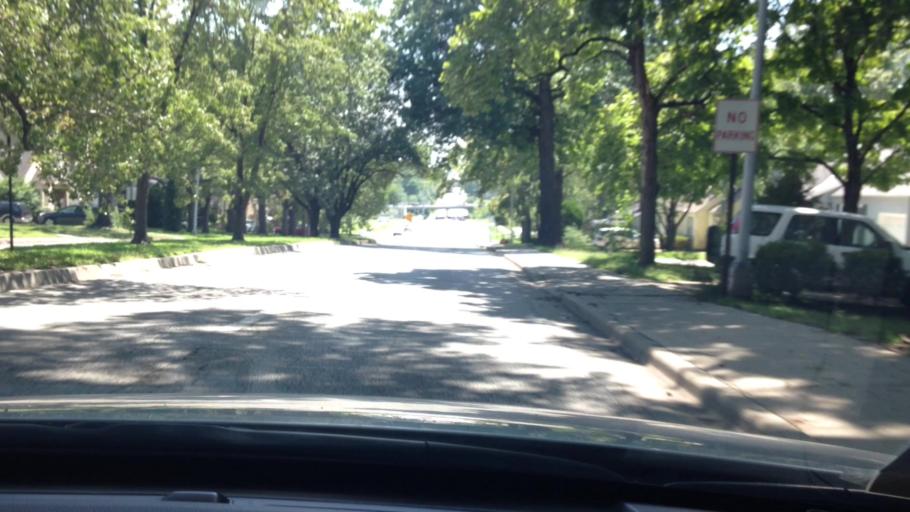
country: US
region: Kansas
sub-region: Johnson County
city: Fairway
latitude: 39.0280
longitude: -94.6398
